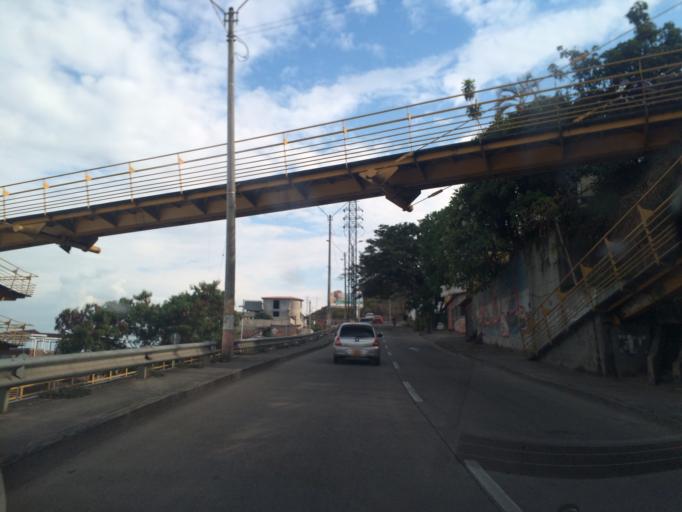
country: CO
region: Valle del Cauca
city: Cali
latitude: 3.4428
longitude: -76.5487
